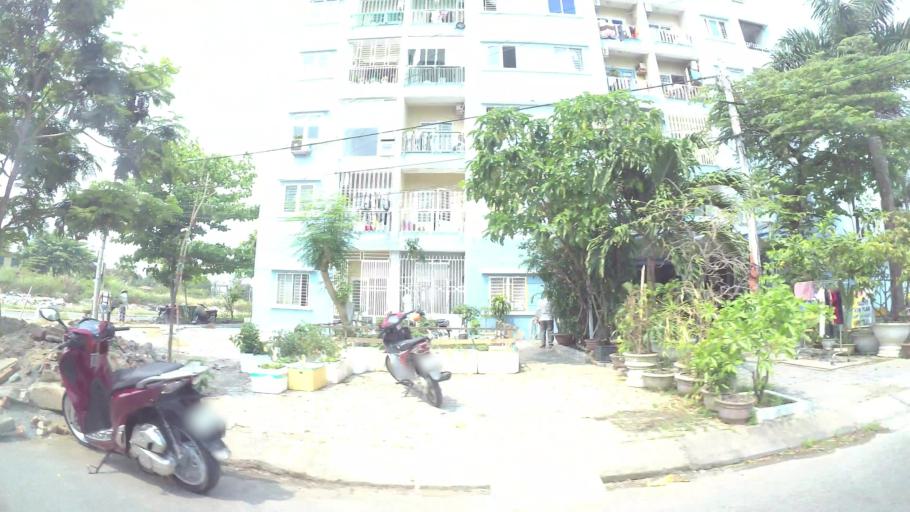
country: VN
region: Da Nang
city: Da Nang
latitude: 16.0880
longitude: 108.2309
